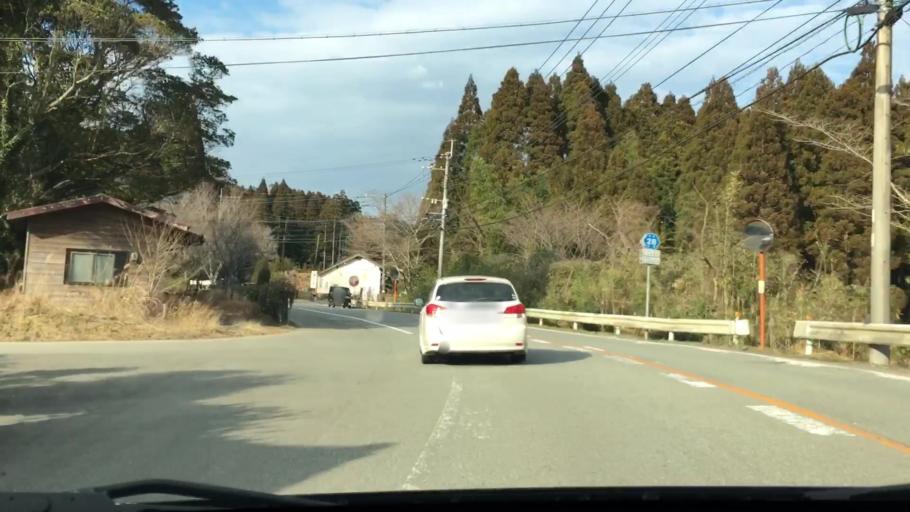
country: JP
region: Miyazaki
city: Nichinan
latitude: 31.7255
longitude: 131.3306
